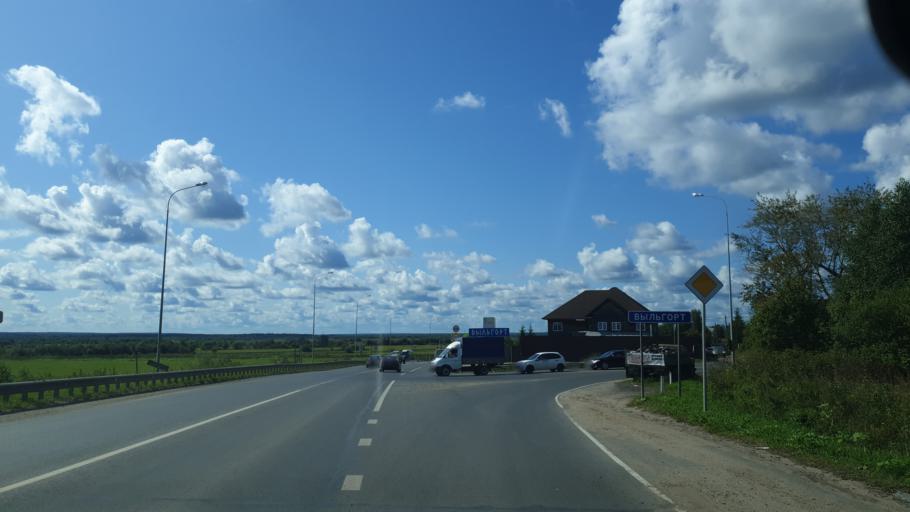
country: RU
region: Komi Republic
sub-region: Syktyvdinskiy Rayon
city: Syktyvkar
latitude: 61.6343
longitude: 50.8100
